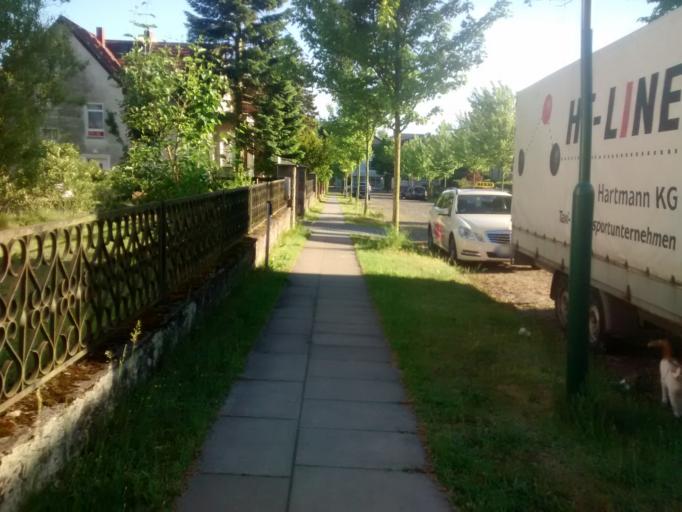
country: DE
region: Brandenburg
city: Hohen Neuendorf
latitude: 52.6695
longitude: 13.2918
